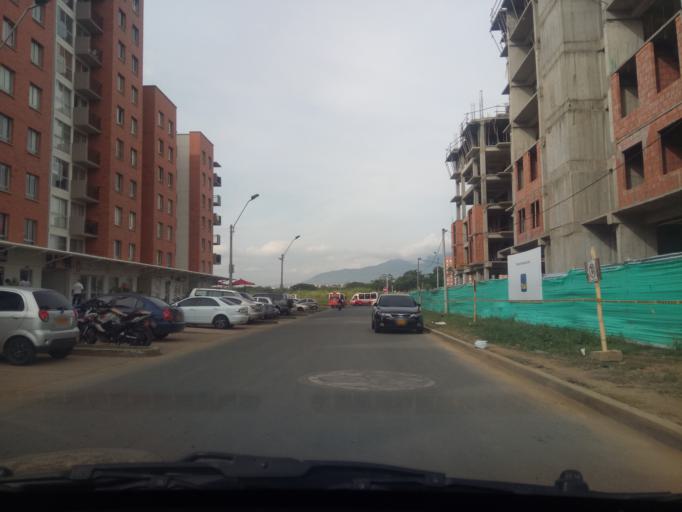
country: CO
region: Valle del Cauca
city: Cali
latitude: 3.3668
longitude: -76.5084
